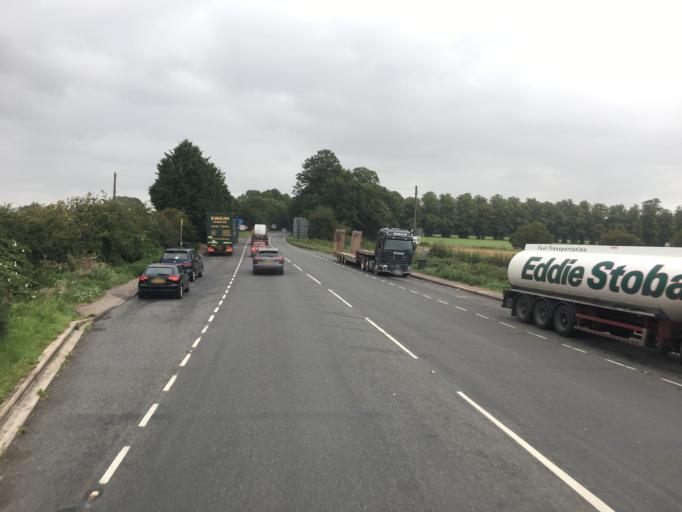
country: GB
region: England
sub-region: Warwickshire
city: Rugby
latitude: 52.4094
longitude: -1.2456
